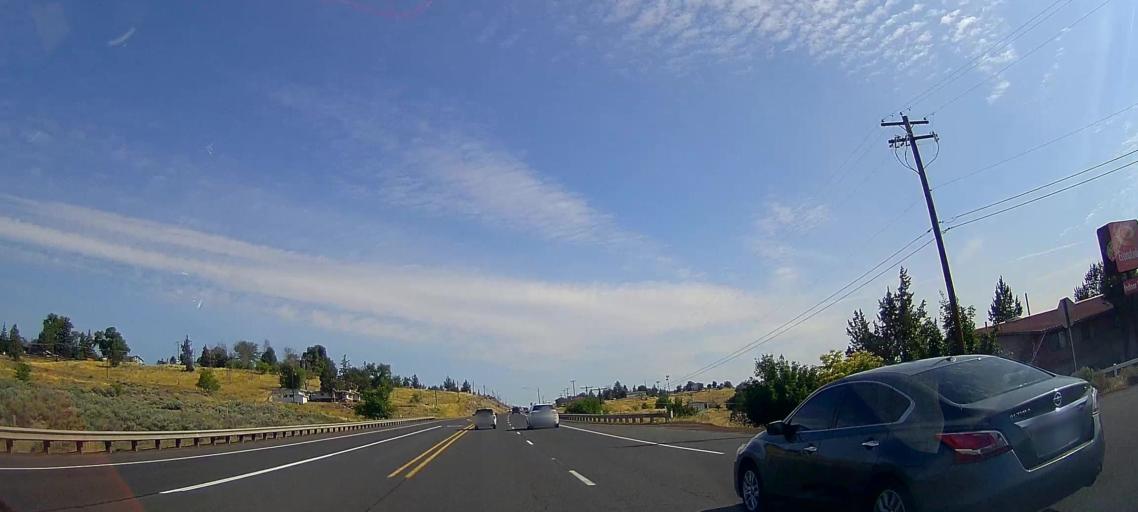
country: US
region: Oregon
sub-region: Jefferson County
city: Madras
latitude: 44.6455
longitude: -121.1295
